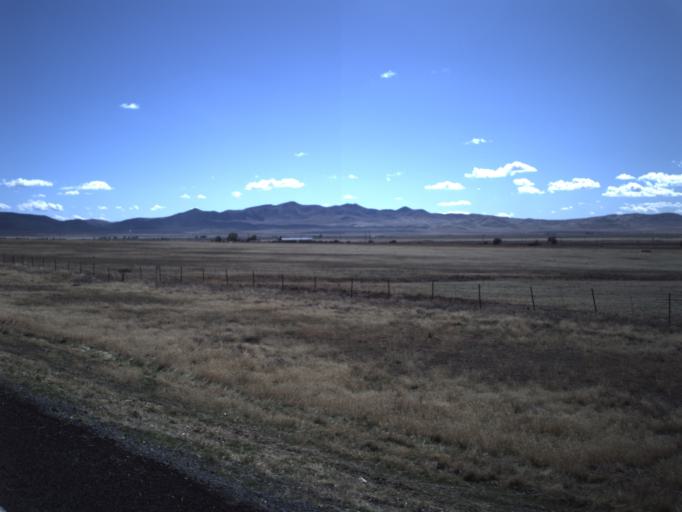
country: US
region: Utah
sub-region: Beaver County
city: Milford
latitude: 38.2714
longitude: -112.9581
